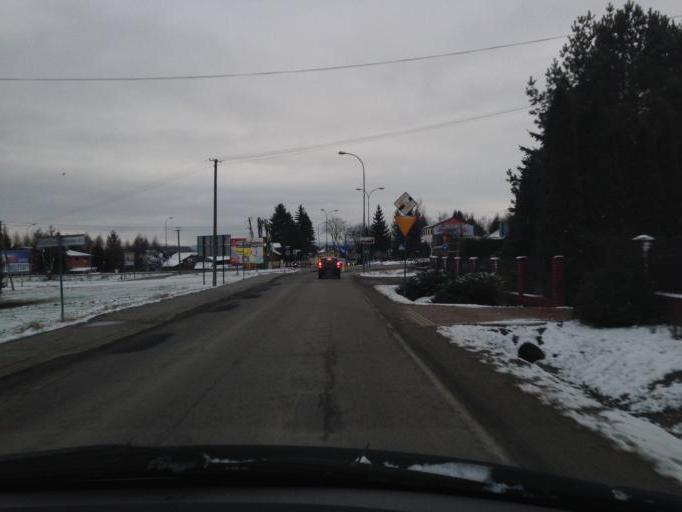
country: PL
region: Lesser Poland Voivodeship
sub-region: Powiat gorlicki
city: Moszczenica
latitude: 49.7050
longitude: 21.1171
